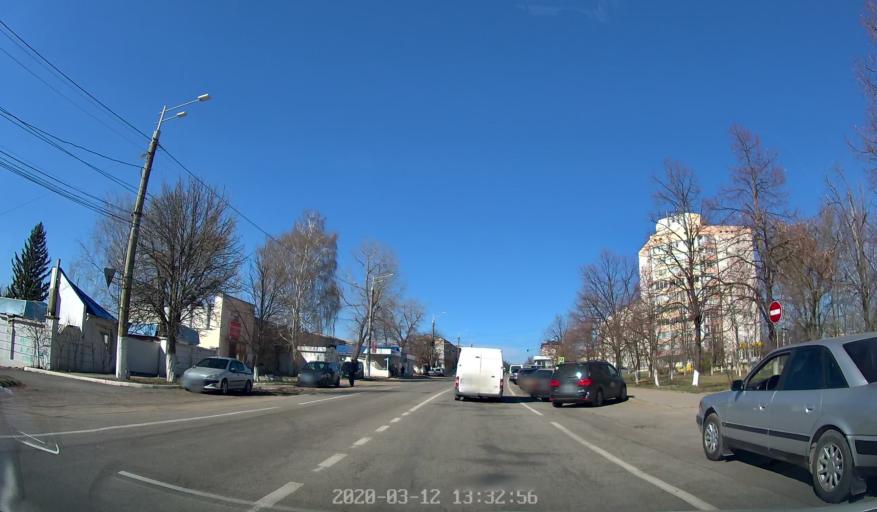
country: MD
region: Laloveni
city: Ialoveni
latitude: 46.9539
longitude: 28.7702
